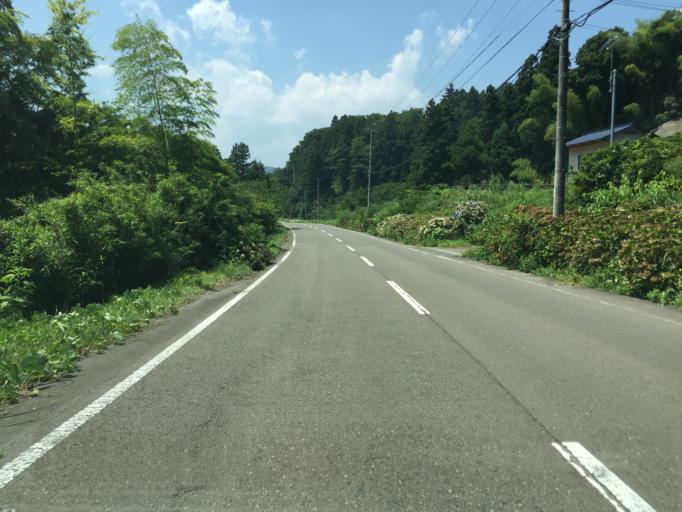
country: JP
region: Miyagi
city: Marumori
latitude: 37.9346
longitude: 140.7162
